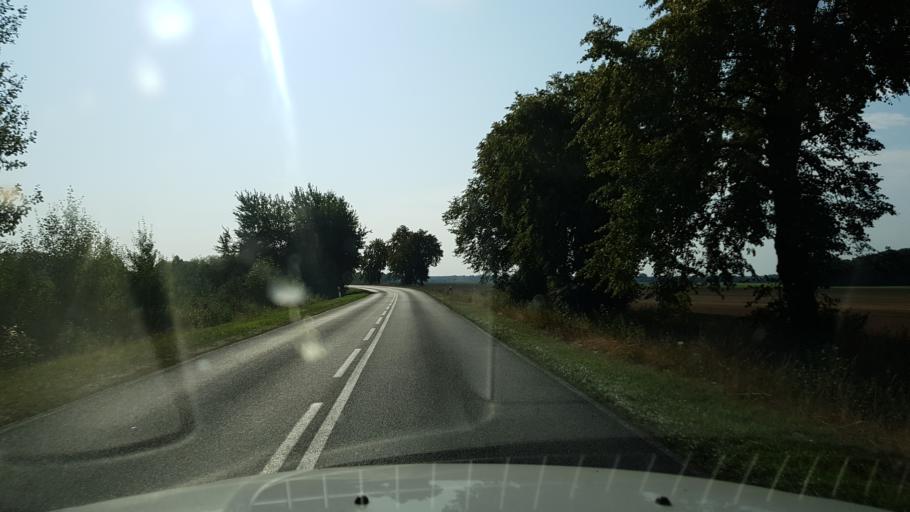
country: PL
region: West Pomeranian Voivodeship
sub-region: Powiat gryficki
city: Ploty
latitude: 53.7931
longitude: 15.2850
